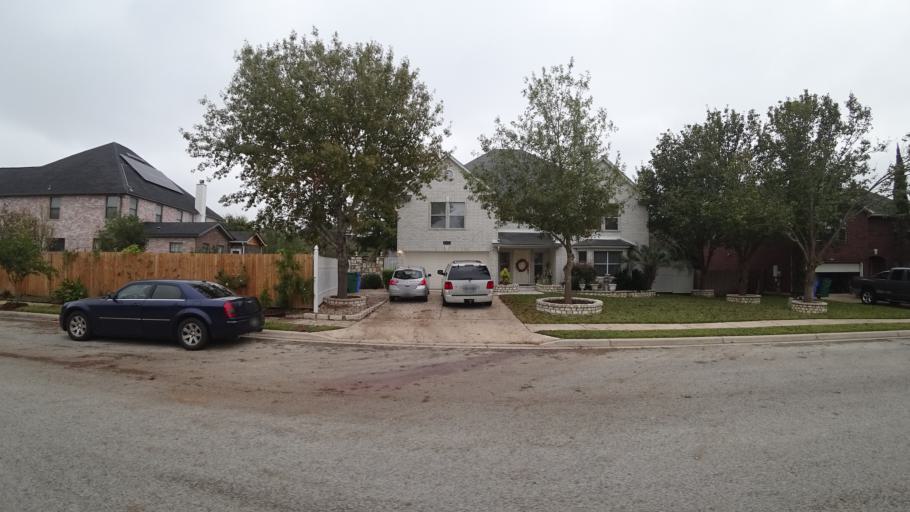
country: US
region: Texas
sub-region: Travis County
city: Pflugerville
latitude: 30.4254
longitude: -97.6206
